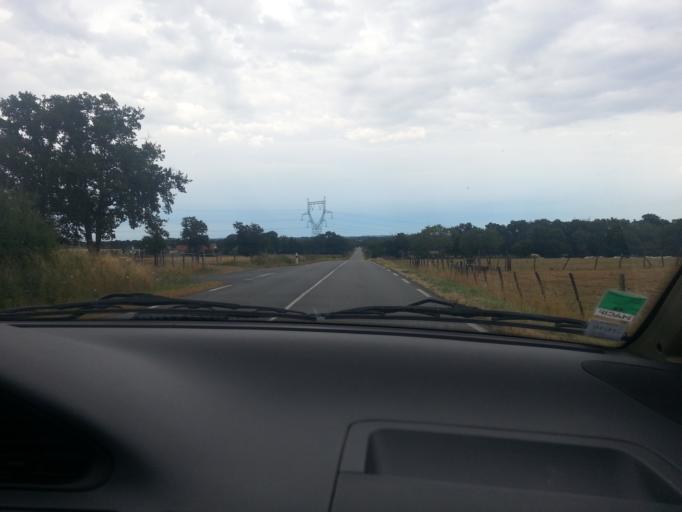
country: FR
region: Auvergne
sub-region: Departement de l'Allier
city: Saint-Gerand-le-Puy
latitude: 46.2101
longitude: 3.5204
